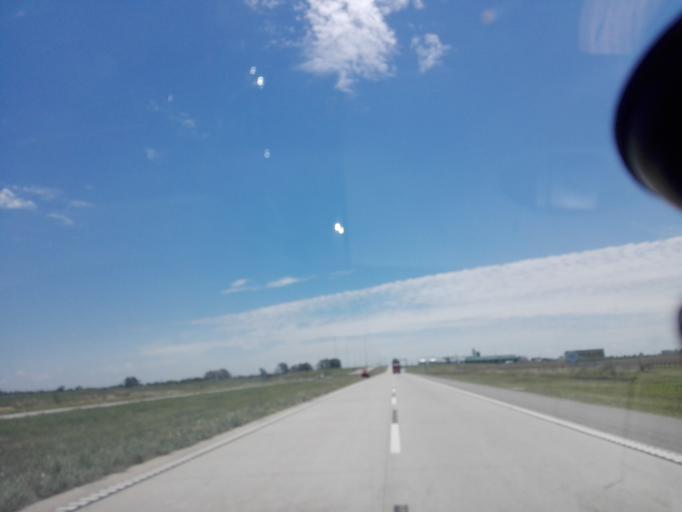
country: AR
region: Cordoba
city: Villa Maria
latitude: -32.4238
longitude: -63.1495
